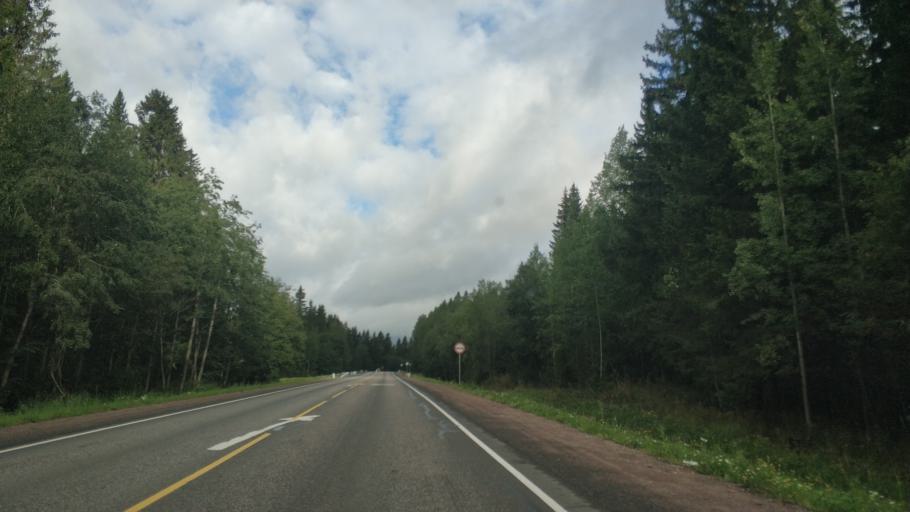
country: RU
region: Republic of Karelia
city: Khelyulya
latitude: 61.7861
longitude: 30.6399
